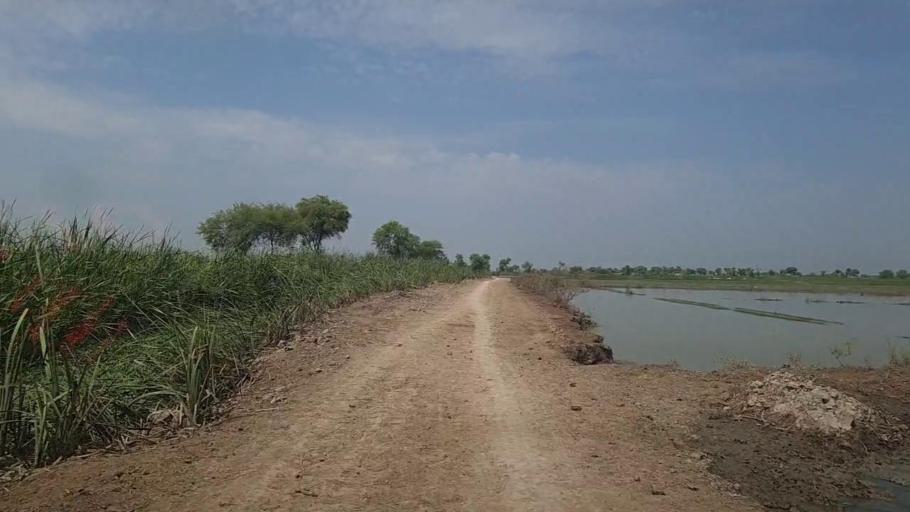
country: PK
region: Sindh
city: Thul
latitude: 28.3037
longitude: 68.6746
